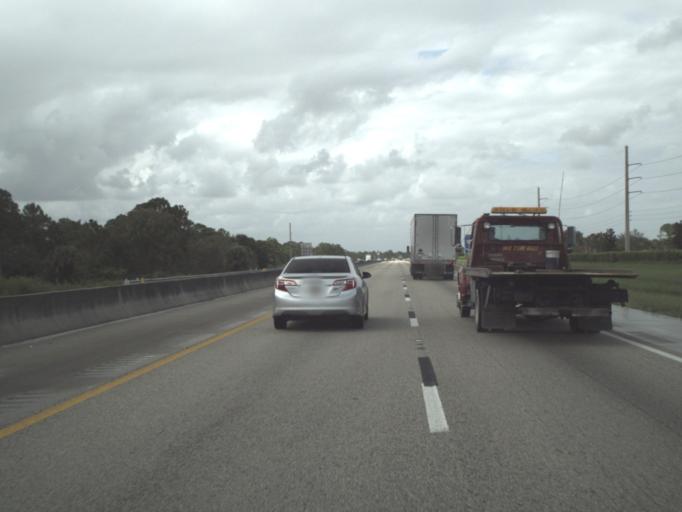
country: US
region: Florida
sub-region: Martin County
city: Palm City
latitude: 27.1827
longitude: -80.3190
